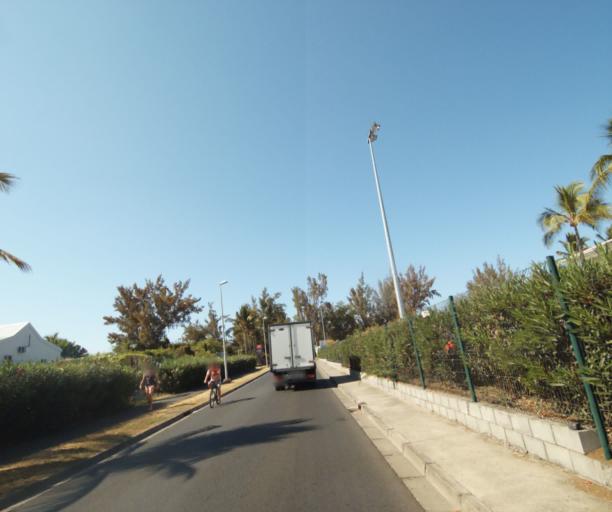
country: RE
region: Reunion
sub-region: Reunion
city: Saint-Paul
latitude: -21.0673
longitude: 55.2228
